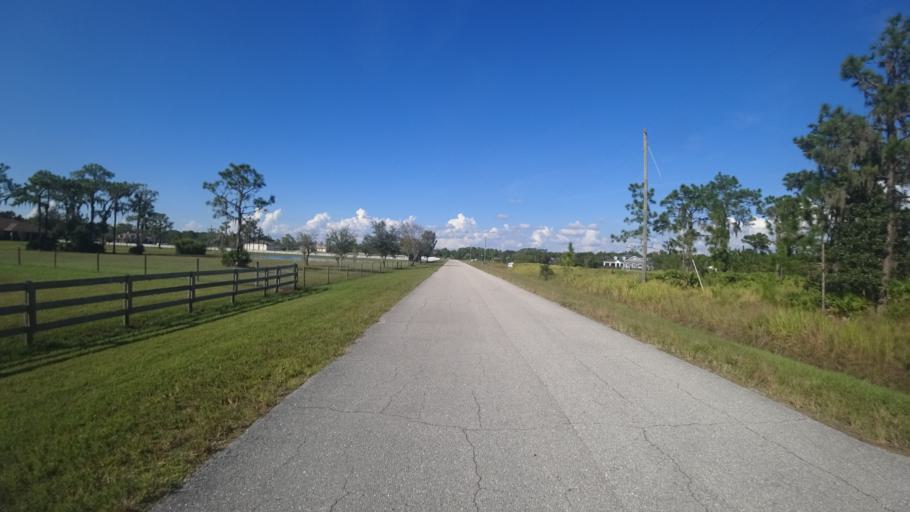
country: US
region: Florida
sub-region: Sarasota County
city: Lake Sarasota
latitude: 27.3929
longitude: -82.2835
